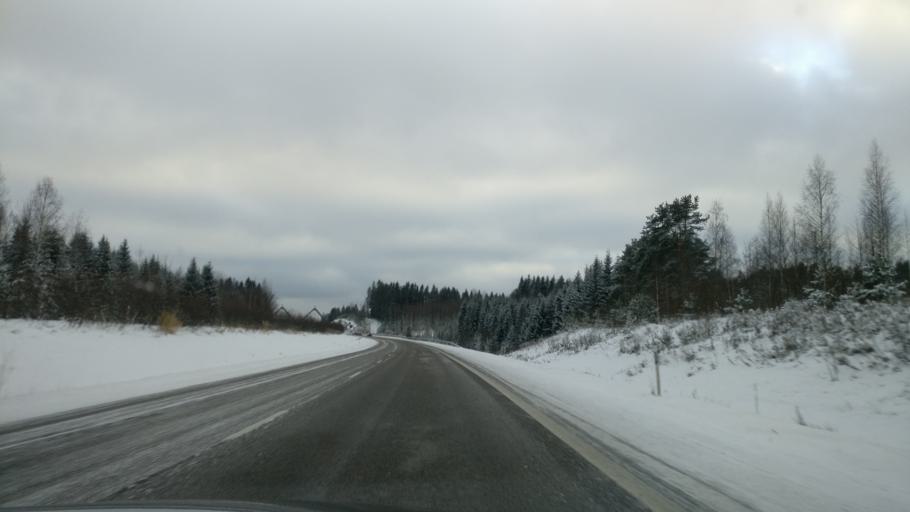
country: FI
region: Paijanne Tavastia
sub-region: Lahti
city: Nastola
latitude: 61.0928
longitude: 25.8971
